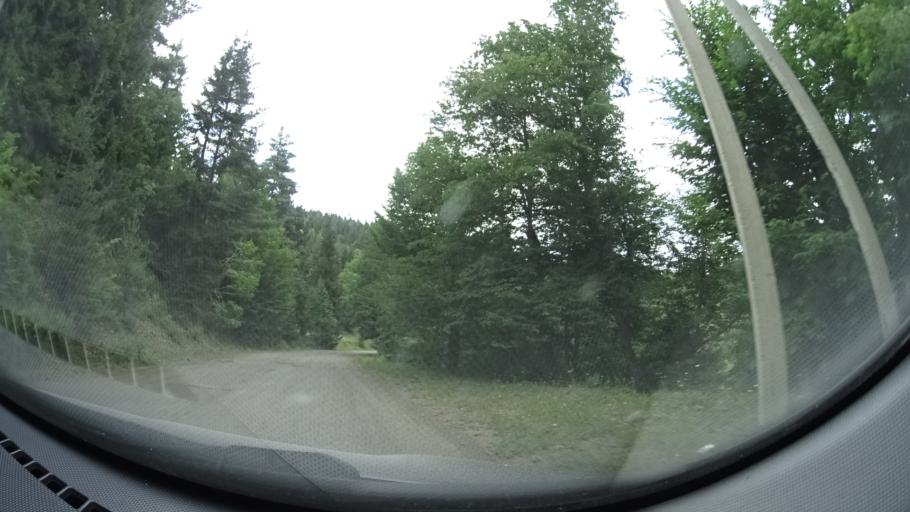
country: GE
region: Samtskhe-Javakheti
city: Adigeni
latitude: 41.6666
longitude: 42.6165
